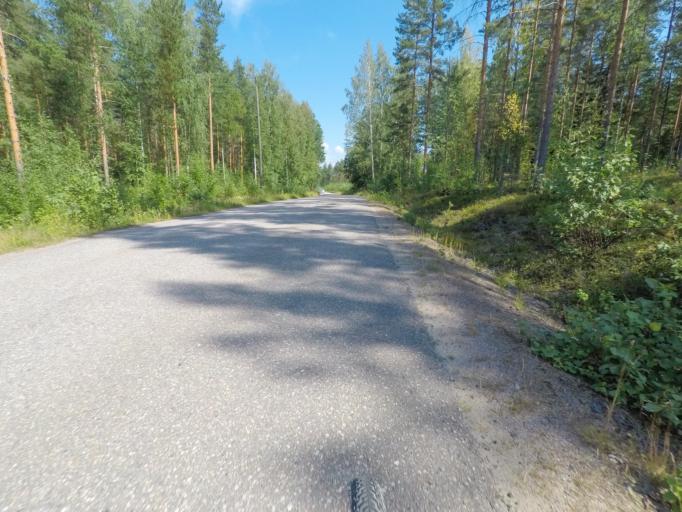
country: FI
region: Southern Savonia
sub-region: Mikkeli
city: Puumala
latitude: 61.4222
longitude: 28.1405
